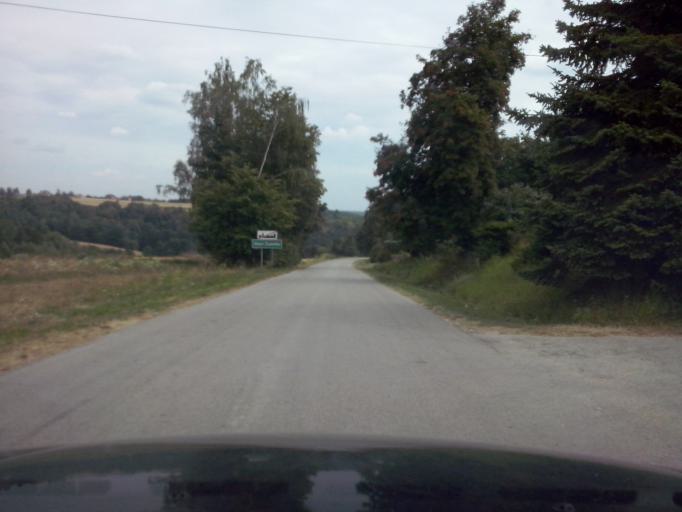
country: PL
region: Swietokrzyskie
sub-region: Powiat kielecki
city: Lagow
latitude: 50.7186
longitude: 21.1358
